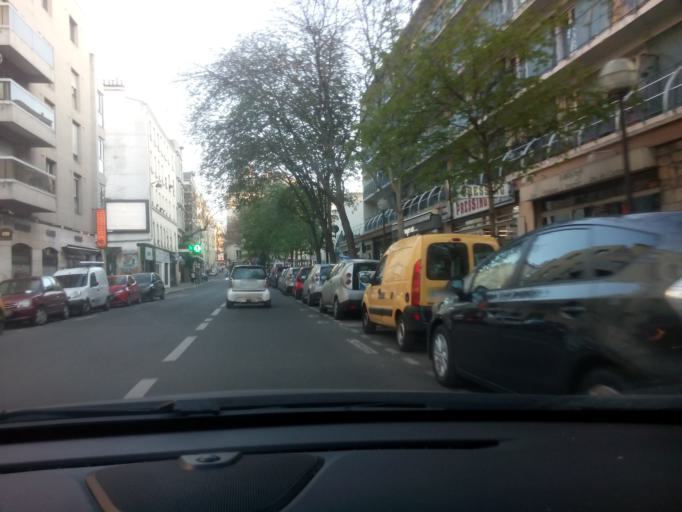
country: FR
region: Ile-de-France
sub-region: Paris
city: Paris
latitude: 48.8408
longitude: 2.3560
